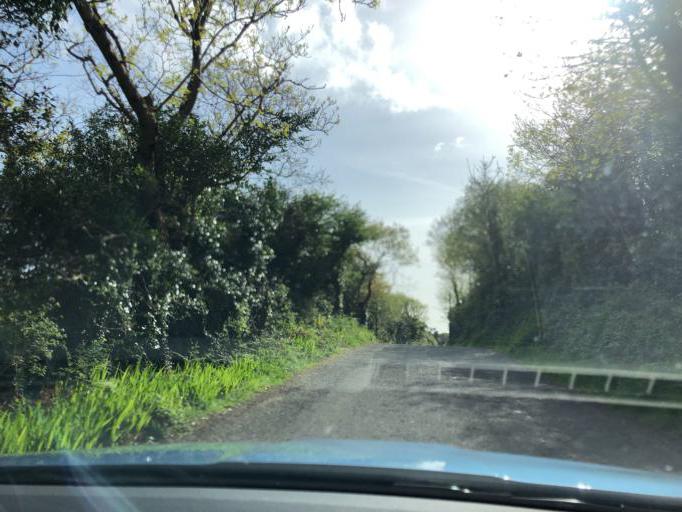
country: IE
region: Munster
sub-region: Ciarrai
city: Cahersiveen
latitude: 51.7616
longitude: -10.1363
